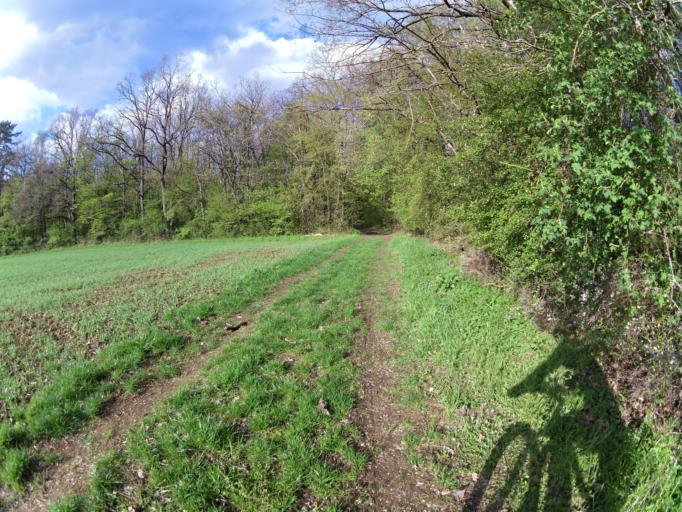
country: DE
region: Bavaria
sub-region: Regierungsbezirk Unterfranken
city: Greussenheim
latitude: 49.7874
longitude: 9.7829
